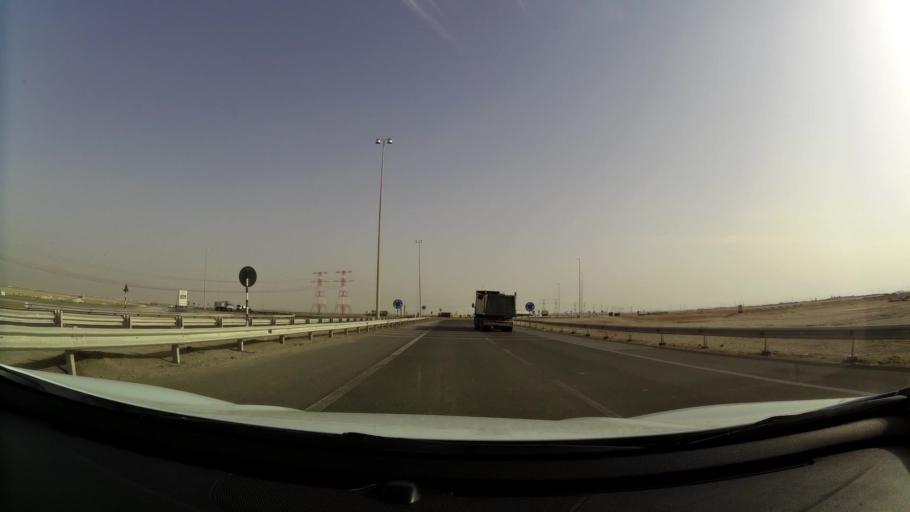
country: AE
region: Abu Dhabi
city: Abu Dhabi
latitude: 24.2048
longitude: 54.4192
